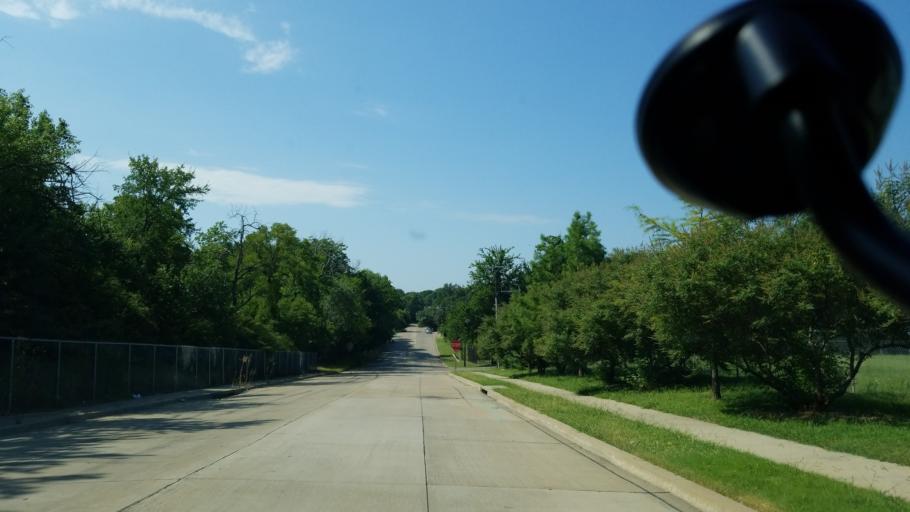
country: US
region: Texas
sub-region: Dallas County
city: Cockrell Hill
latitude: 32.7090
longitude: -96.8659
